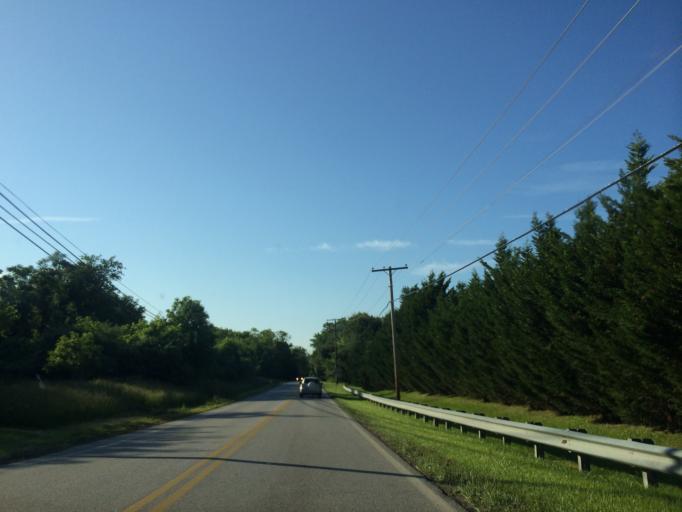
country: US
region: Maryland
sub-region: Howard County
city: Highland
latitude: 39.2622
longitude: -76.9738
